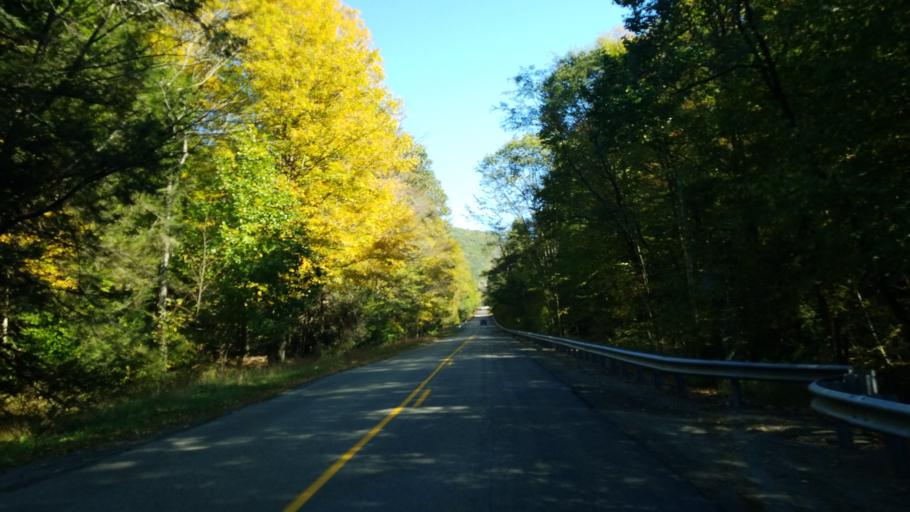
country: US
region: Pennsylvania
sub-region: Elk County
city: Saint Marys
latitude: 41.2662
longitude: -78.4011
